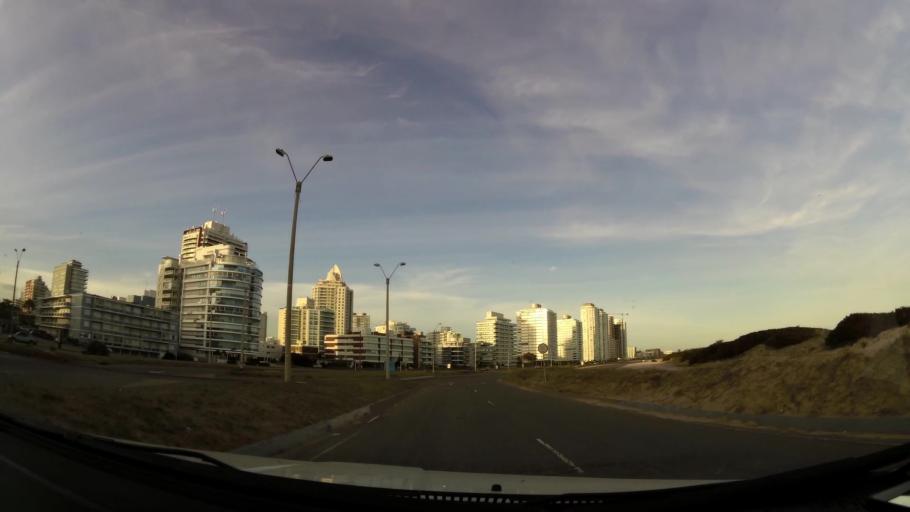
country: UY
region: Maldonado
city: Punta del Este
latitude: -34.9519
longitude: -54.9287
